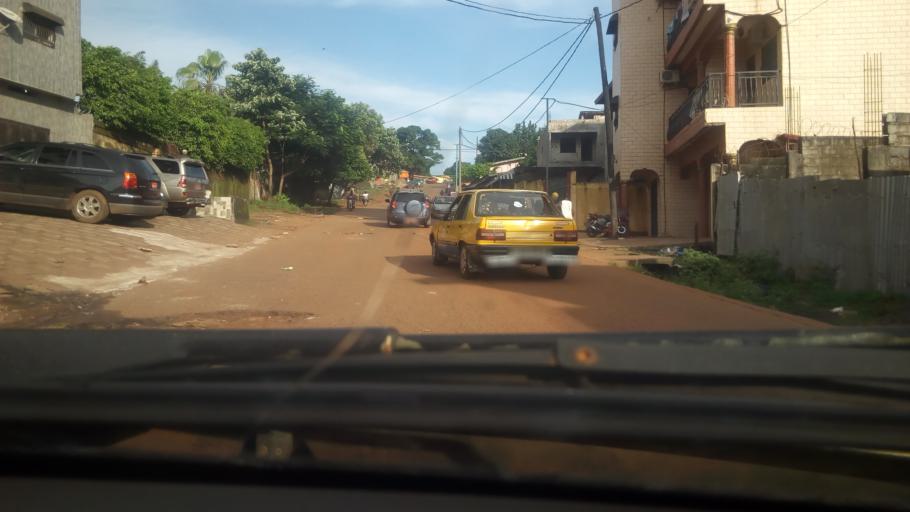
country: GN
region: Conakry
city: Conakry
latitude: 9.6222
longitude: -13.6108
